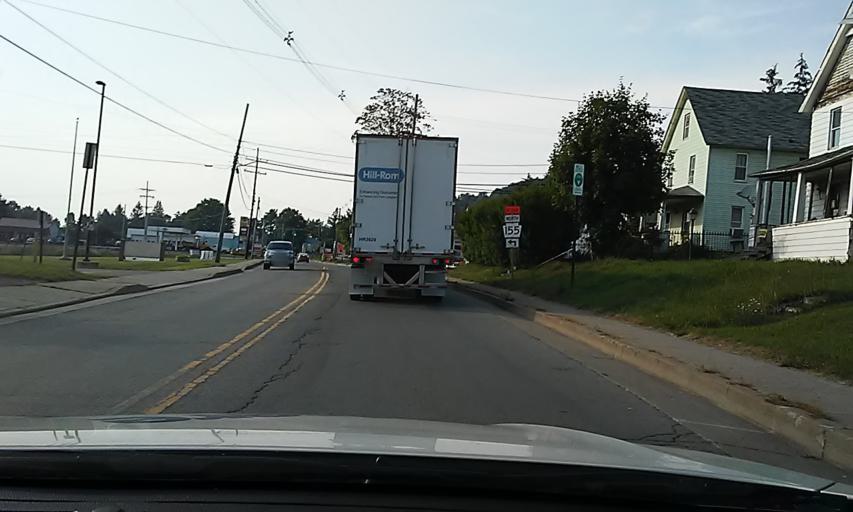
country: US
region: Pennsylvania
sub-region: McKean County
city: Port Allegany
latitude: 41.8190
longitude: -78.2859
